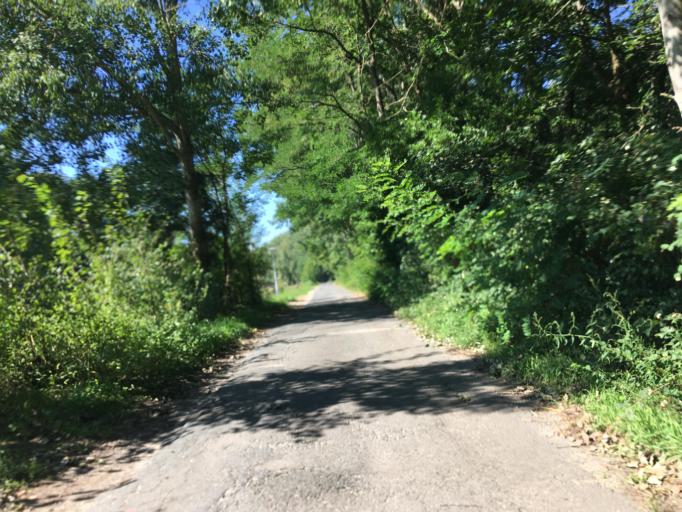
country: DE
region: Brandenburg
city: Gross Koris
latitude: 52.1795
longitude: 13.6653
